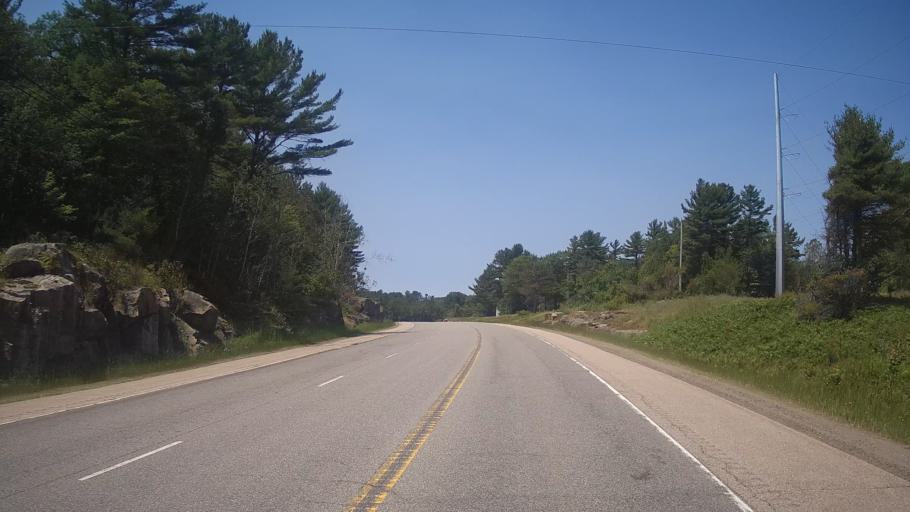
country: CA
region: Ontario
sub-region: Parry Sound District
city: Parry Sound
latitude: 45.5751
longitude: -80.3465
